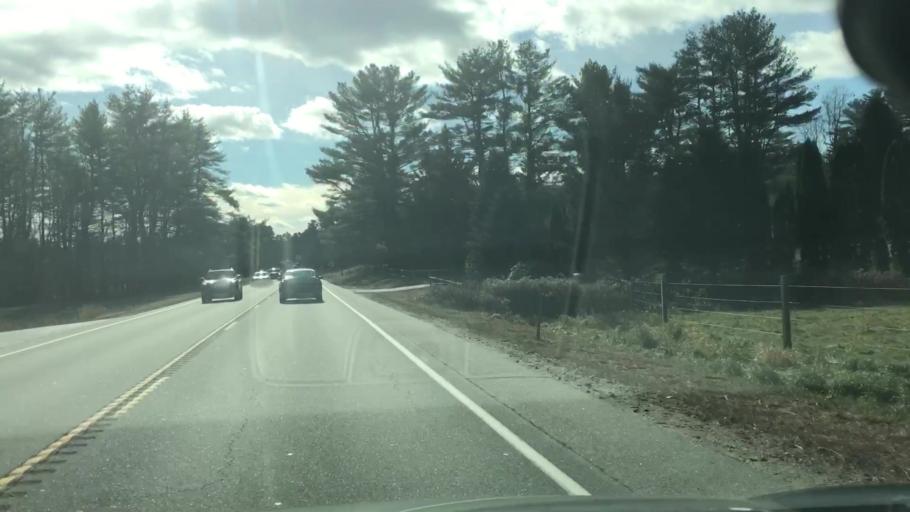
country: US
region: New Hampshire
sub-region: Merrimack County
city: Chichester
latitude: 43.2696
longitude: -71.3696
